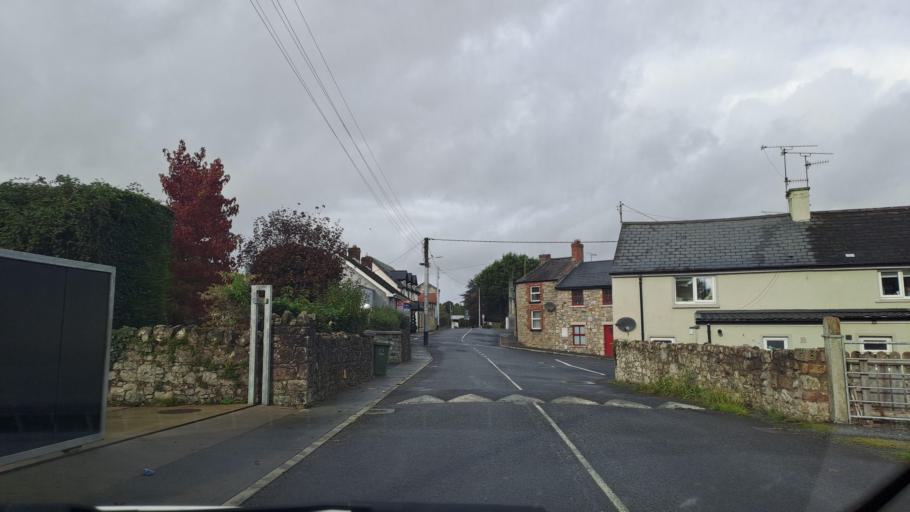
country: IE
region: Ulster
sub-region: County Monaghan
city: Carrickmacross
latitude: 53.9766
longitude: -6.7259
